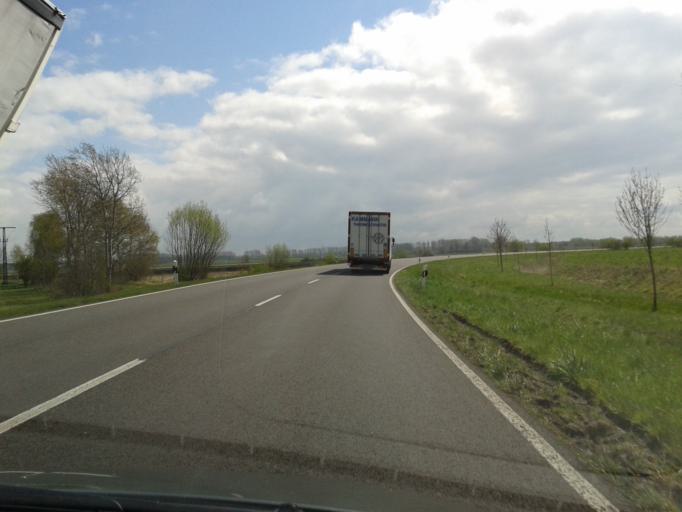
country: DE
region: Saxony-Anhalt
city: Salzwedel
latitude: 52.8660
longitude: 11.1751
